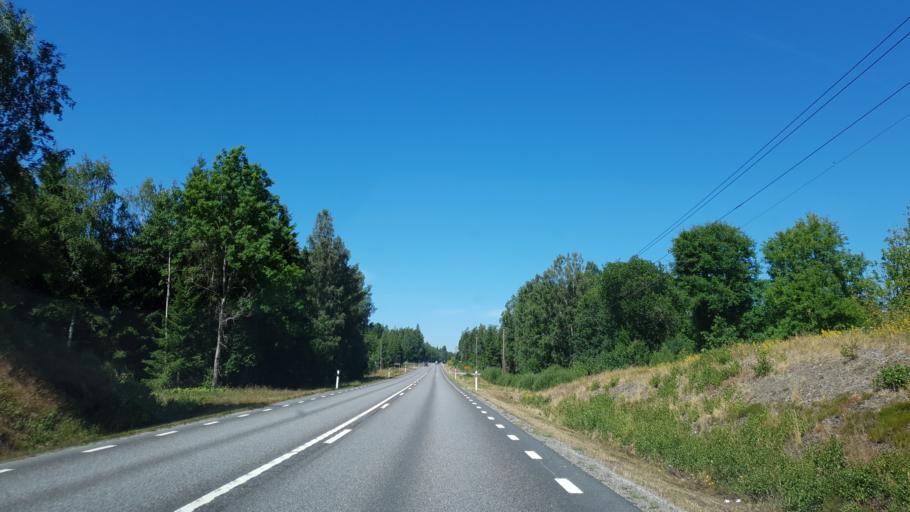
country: SE
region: Joenkoeping
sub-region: Varnamo Kommun
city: Bor
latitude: 57.0539
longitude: 14.2160
